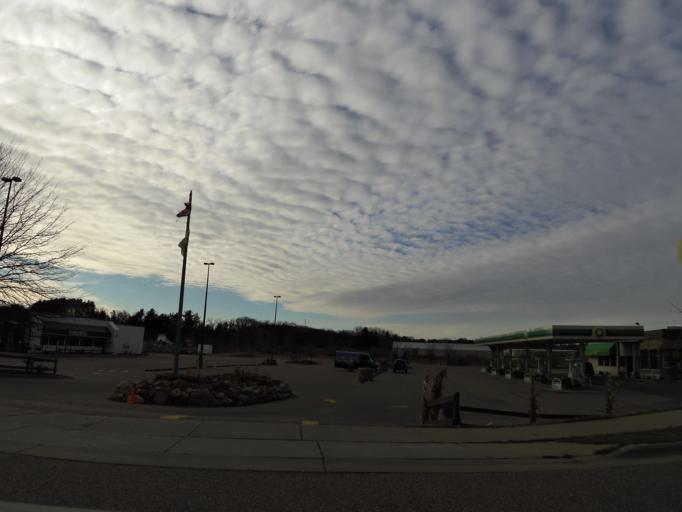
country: US
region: Wisconsin
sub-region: Sauk County
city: Lake Delton
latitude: 43.5807
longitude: -89.7792
